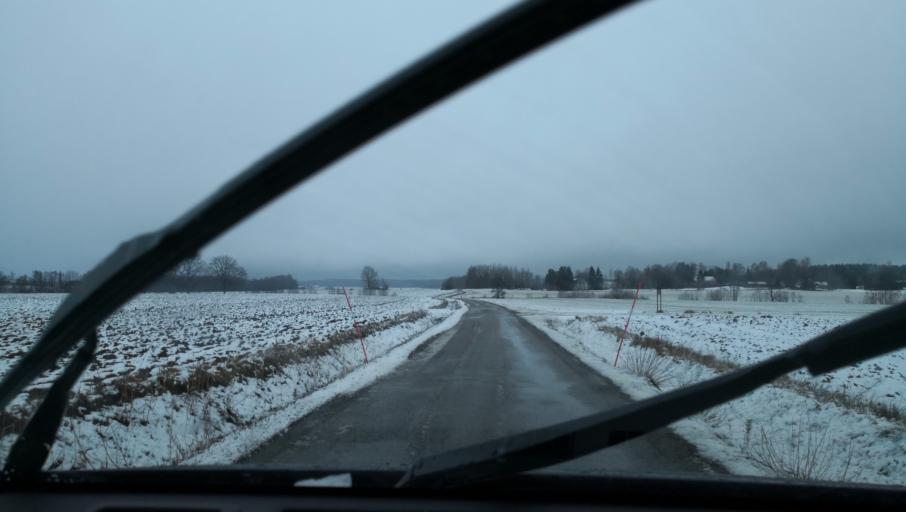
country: SE
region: Vaestmanland
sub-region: Kopings Kommun
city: Kolsva
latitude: 59.5409
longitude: 15.8816
